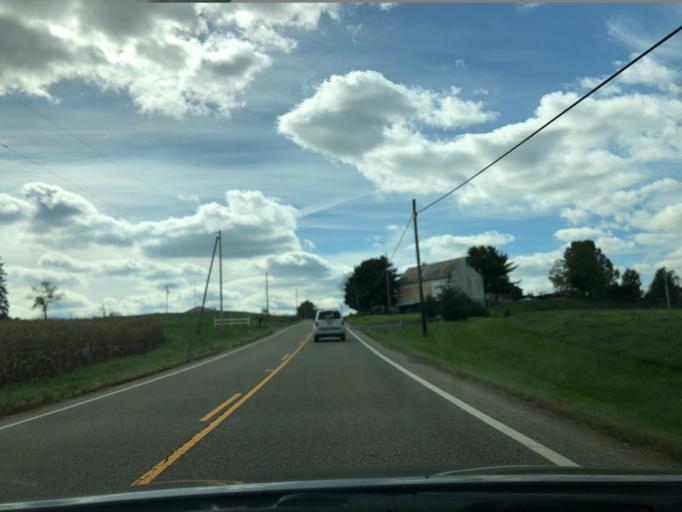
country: US
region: Ohio
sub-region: Stark County
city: Brewster
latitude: 40.6740
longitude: -81.6161
